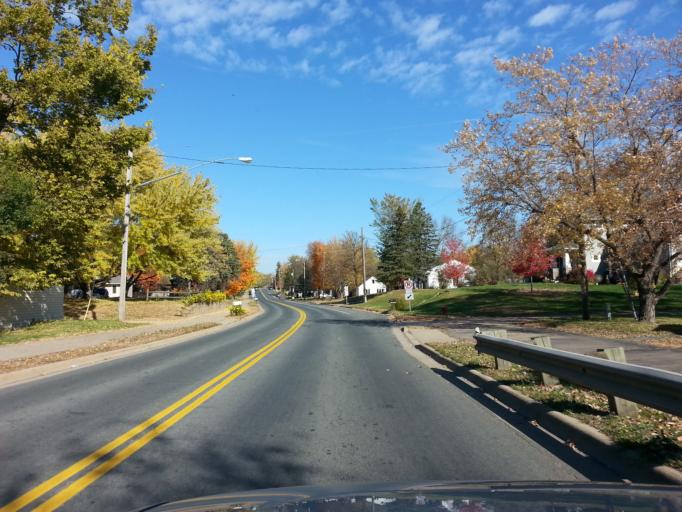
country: US
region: Minnesota
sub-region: Scott County
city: Prior Lake
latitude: 44.7099
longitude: -93.4294
